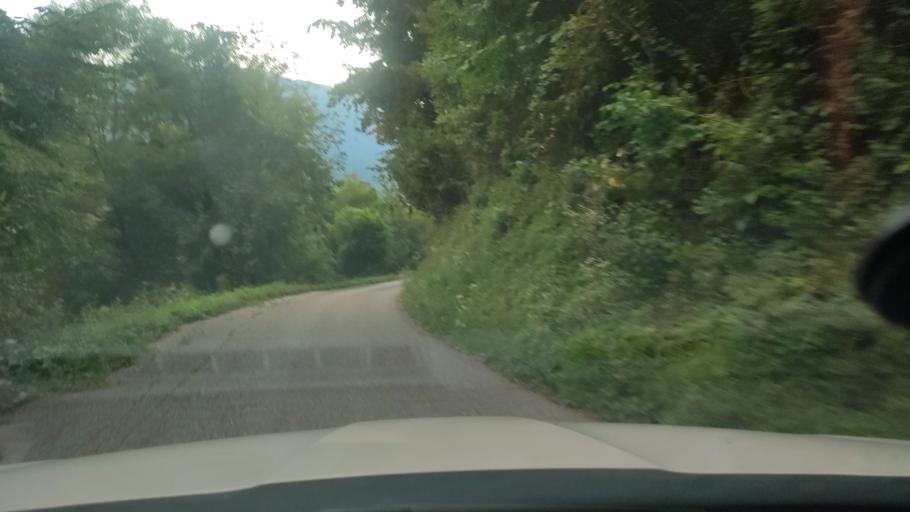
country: IT
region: Friuli Venezia Giulia
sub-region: Provincia di Udine
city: Cras
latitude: 46.2158
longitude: 13.6422
